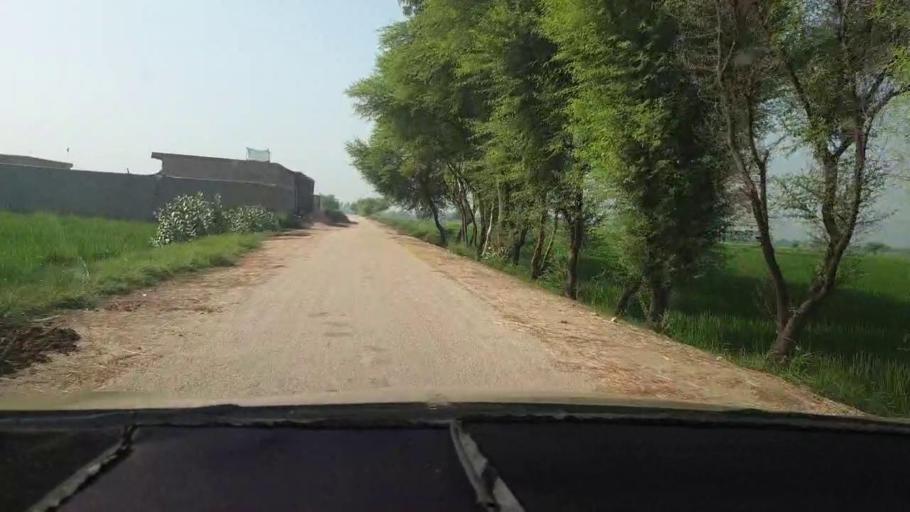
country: PK
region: Sindh
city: Kambar
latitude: 27.6203
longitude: 68.0905
